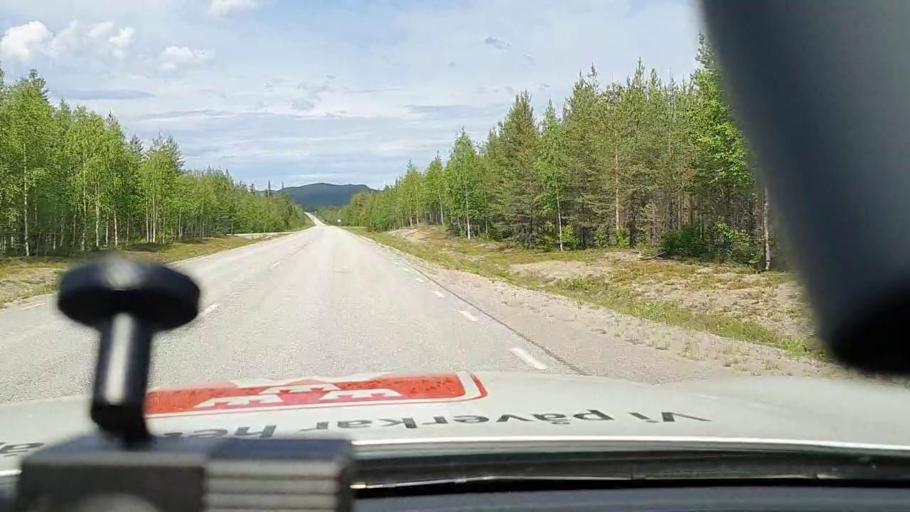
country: SE
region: Norrbotten
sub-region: Jokkmokks Kommun
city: Jokkmokk
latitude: 66.5438
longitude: 20.1387
